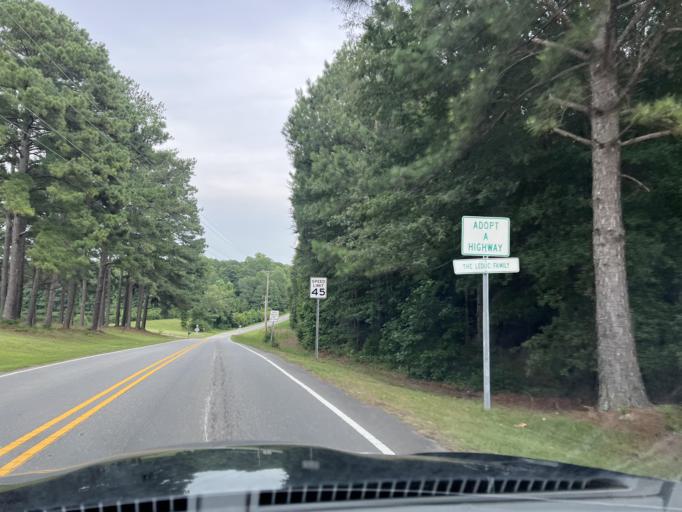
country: US
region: North Carolina
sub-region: Wake County
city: Wake Forest
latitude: 36.0137
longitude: -78.5642
